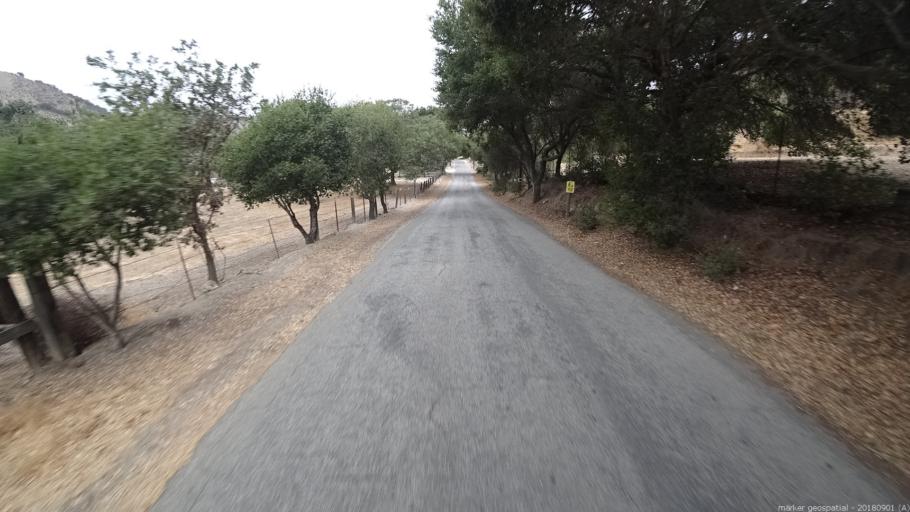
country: US
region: California
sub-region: Monterey County
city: Greenfield
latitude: 36.2704
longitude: -121.3003
